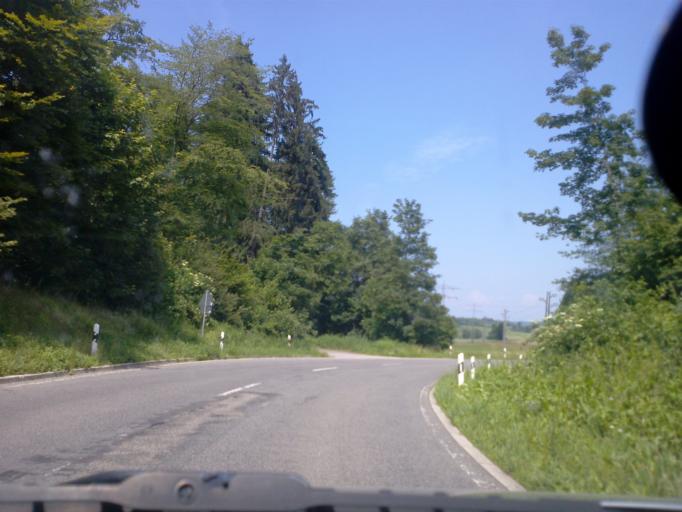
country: DE
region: Baden-Wuerttemberg
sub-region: Karlsruhe Region
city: Bretten
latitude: 49.0121
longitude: 8.6788
